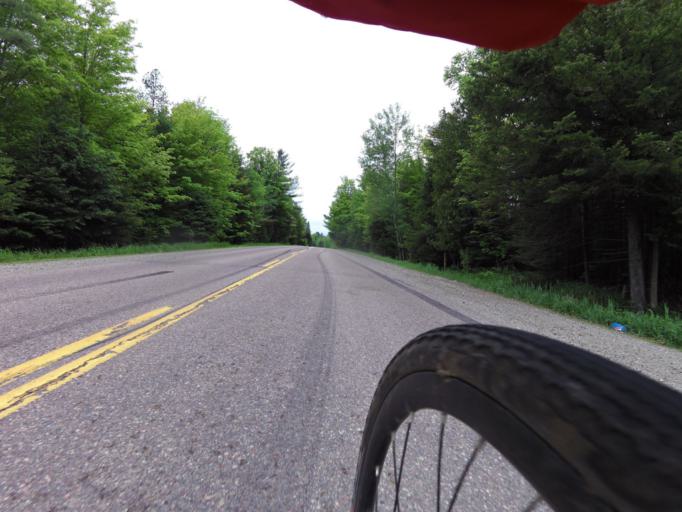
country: CA
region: Ontario
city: Renfrew
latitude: 45.2875
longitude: -76.6850
